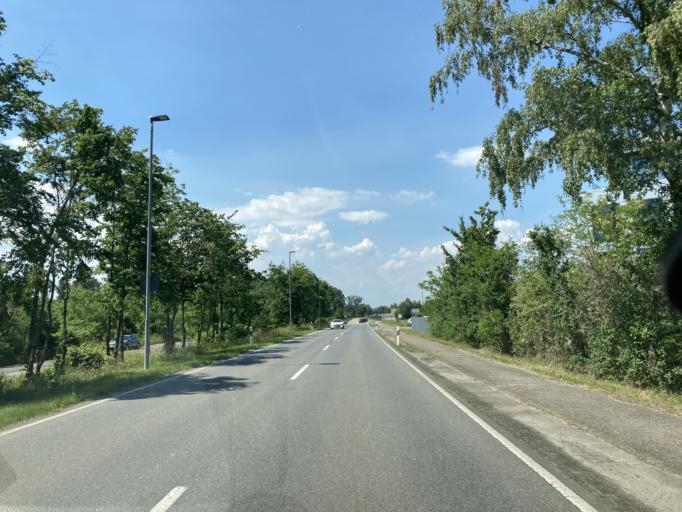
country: DE
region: Baden-Wuerttemberg
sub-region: Karlsruhe Region
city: Graben-Neudorf
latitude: 49.1793
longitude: 8.4902
